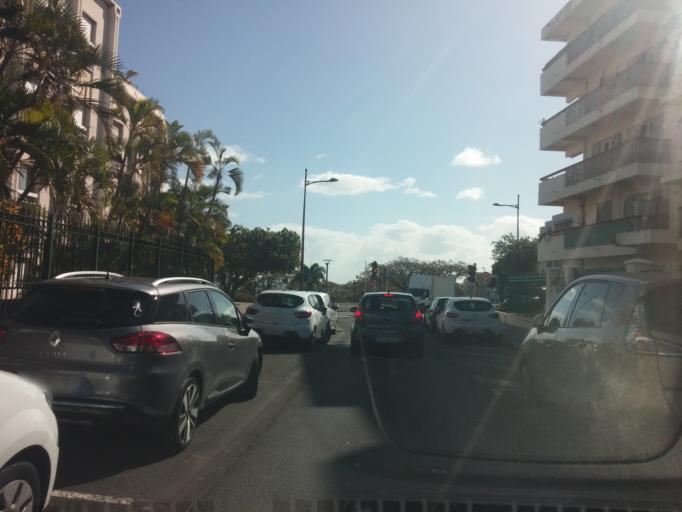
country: RE
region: Reunion
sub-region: Reunion
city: Saint-Denis
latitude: -20.8854
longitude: 55.4470
